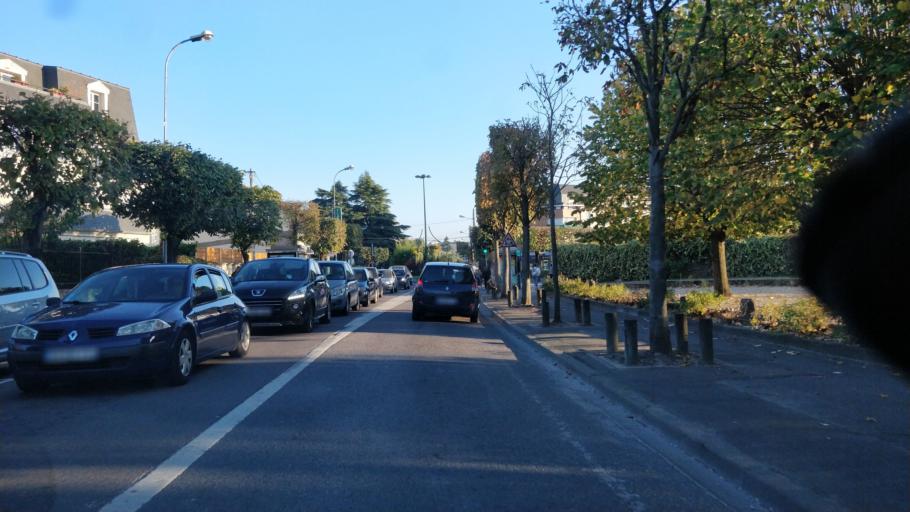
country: FR
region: Ile-de-France
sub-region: Departement de Seine-Saint-Denis
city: Gournay-sur-Marne
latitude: 48.8620
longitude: 2.5788
